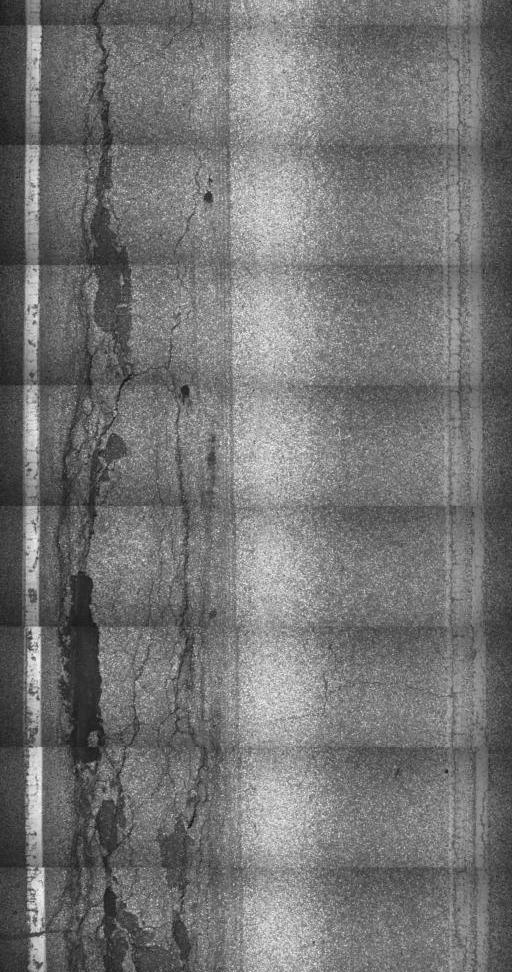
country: US
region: Vermont
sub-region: Washington County
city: South Barre
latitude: 44.1450
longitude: -72.4344
